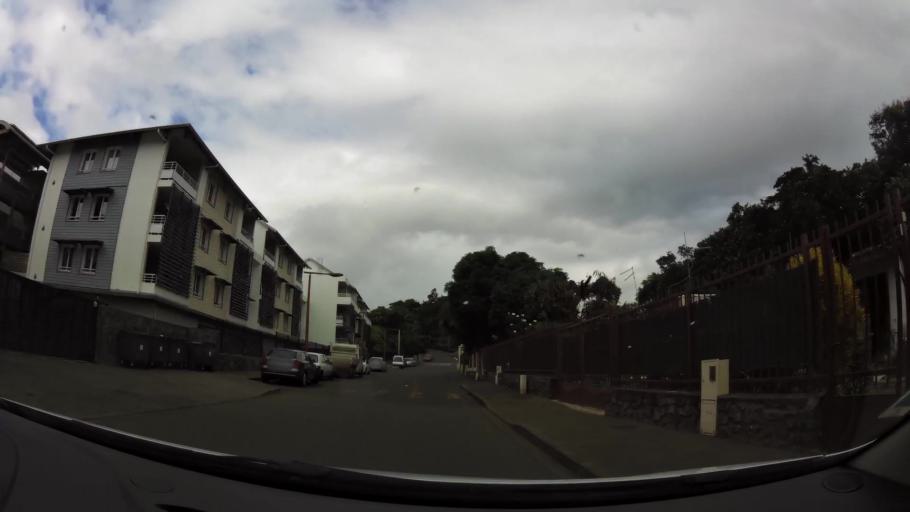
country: RE
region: Reunion
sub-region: Reunion
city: Sainte-Marie
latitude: -20.8972
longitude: 55.5513
